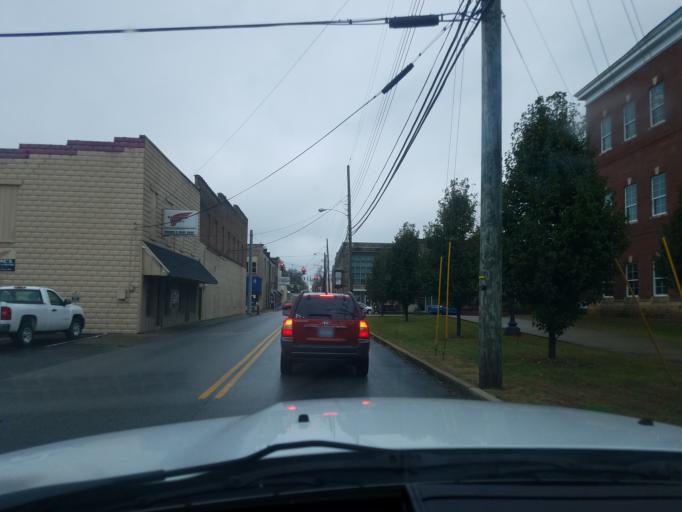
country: US
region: Kentucky
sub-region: Taylor County
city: Campbellsville
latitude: 37.3409
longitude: -85.3429
